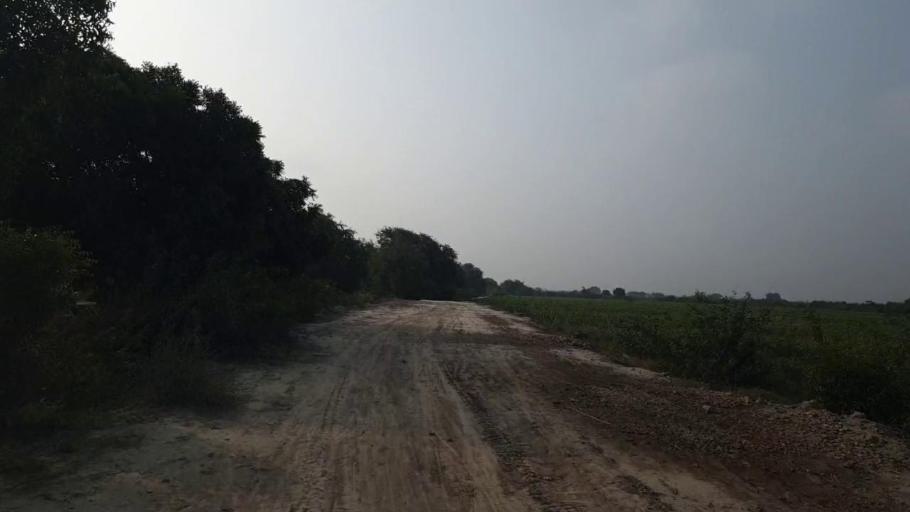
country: PK
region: Sindh
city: Tando Muhammad Khan
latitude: 25.1612
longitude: 68.5957
